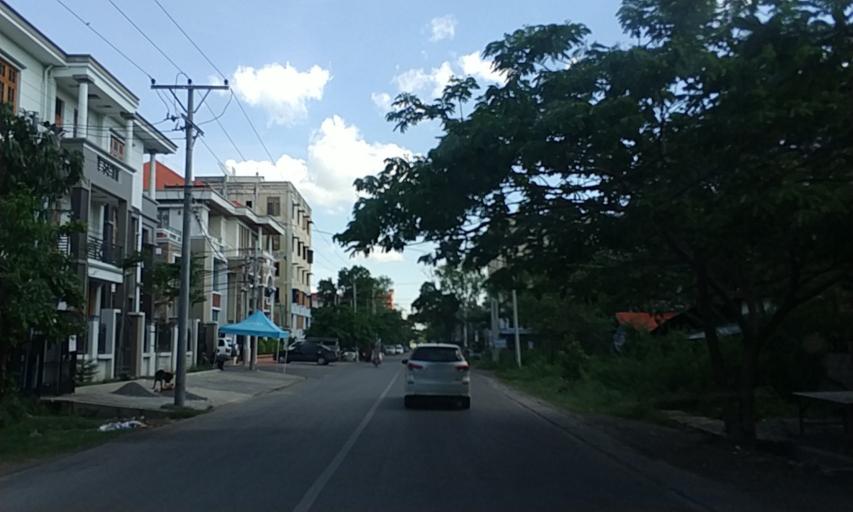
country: MM
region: Mandalay
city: Mandalay
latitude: 21.9766
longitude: 96.1080
